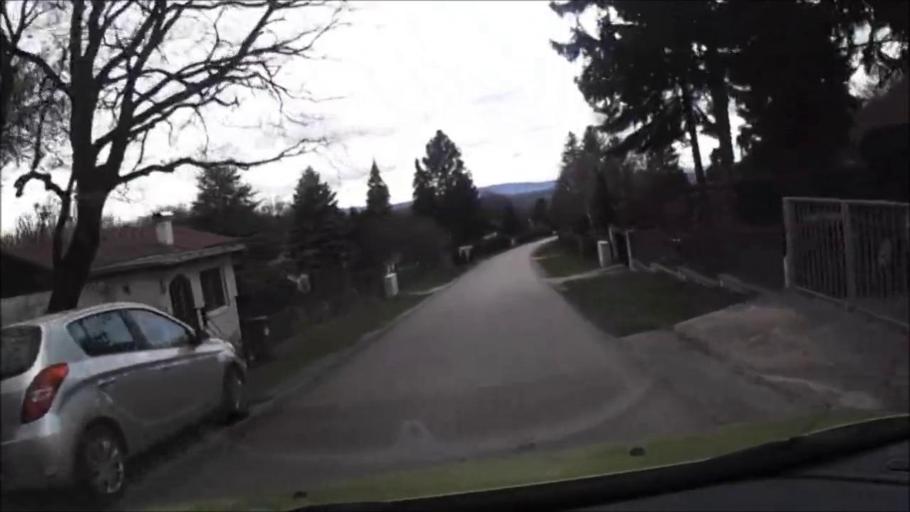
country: AT
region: Burgenland
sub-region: Eisenstadt-Umgebung
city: Loretto
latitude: 47.9017
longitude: 16.5176
